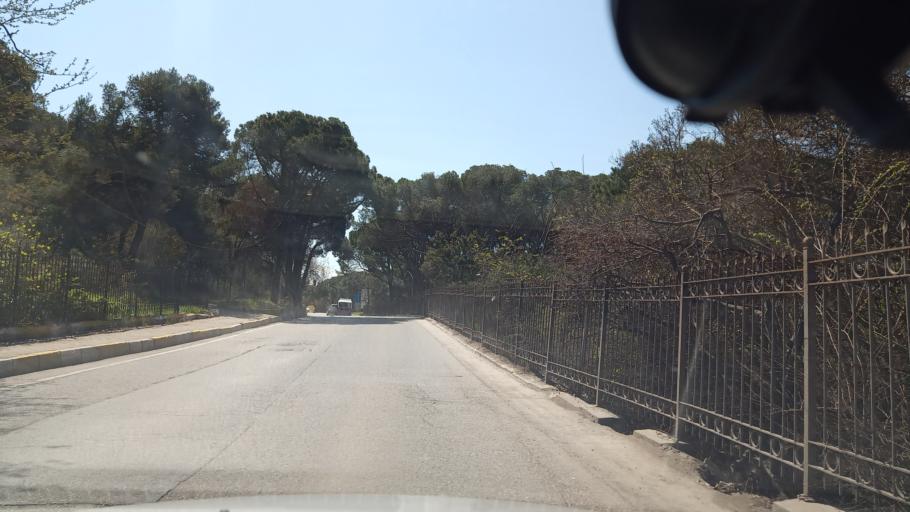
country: TR
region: Istanbul
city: Maltepe
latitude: 40.9517
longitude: 29.1424
